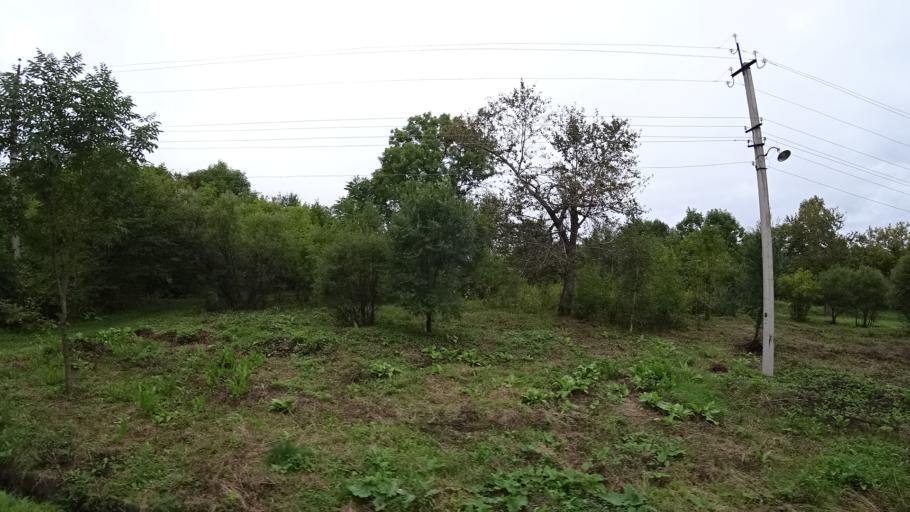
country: RU
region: Primorskiy
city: Rettikhovka
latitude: 44.1684
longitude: 132.7703
